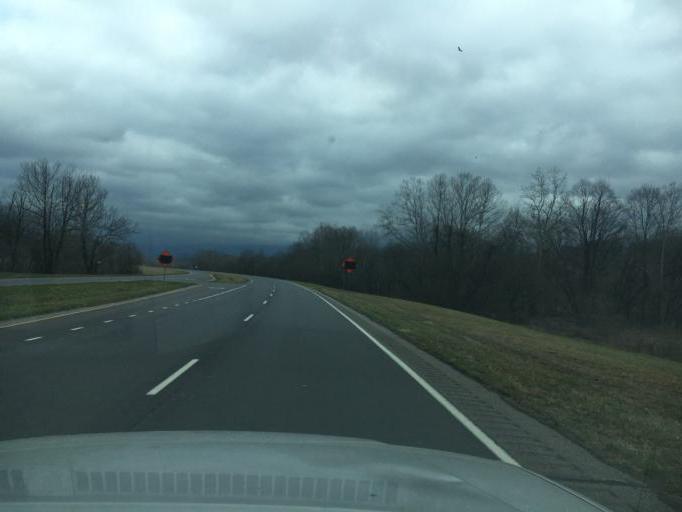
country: US
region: North Carolina
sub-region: Cherokee County
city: Andrews
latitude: 35.1827
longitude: -83.9006
